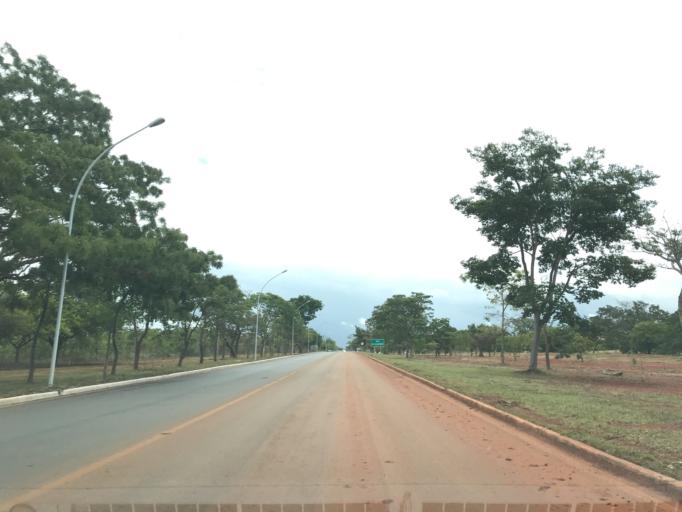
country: BR
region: Federal District
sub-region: Brasilia
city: Brasilia
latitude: -15.7995
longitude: -47.8449
